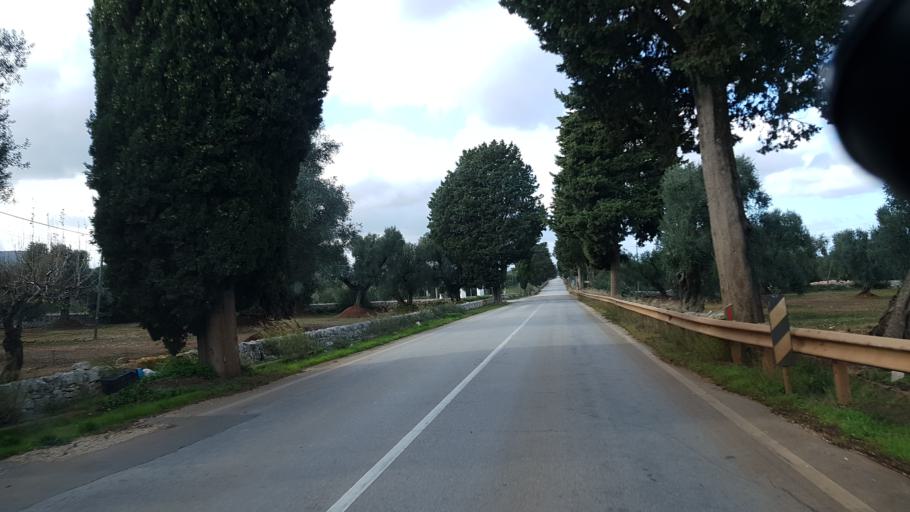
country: IT
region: Apulia
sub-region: Provincia di Brindisi
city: Montalbano
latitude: 40.7627
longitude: 17.5243
